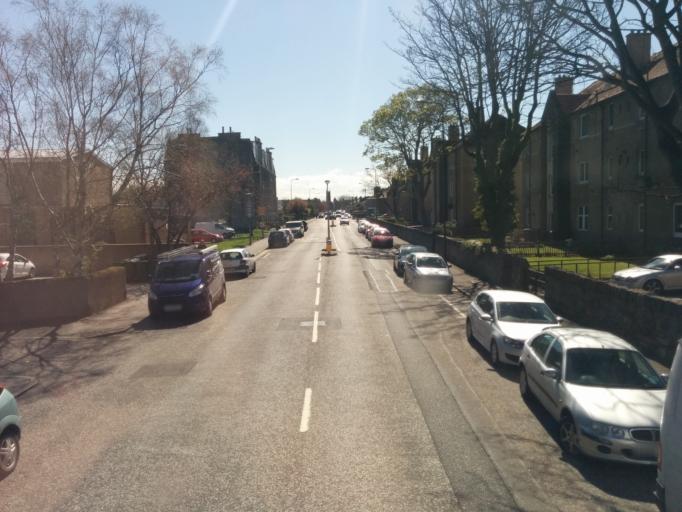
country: GB
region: Scotland
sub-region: Edinburgh
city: Edinburgh
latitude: 55.9765
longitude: -3.2159
